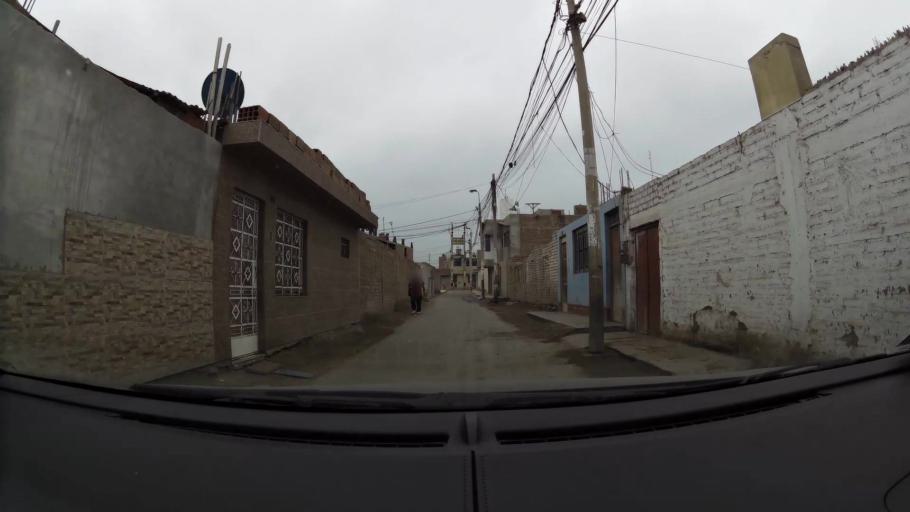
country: PE
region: Lima
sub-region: Barranca
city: Barranca
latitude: -10.7462
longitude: -77.7559
